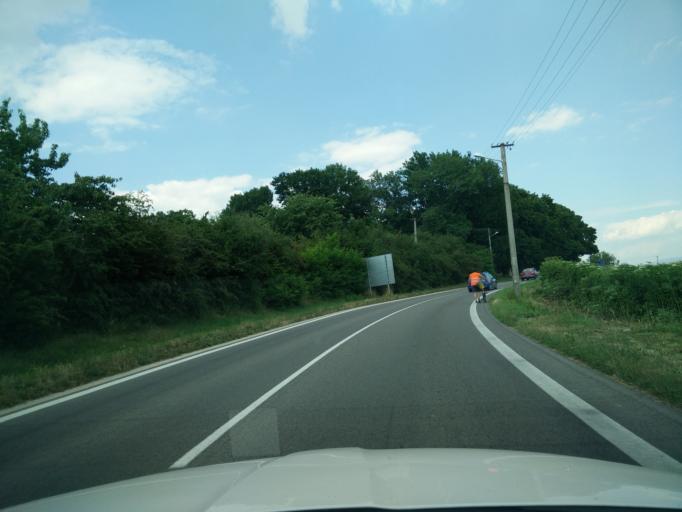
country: SK
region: Nitriansky
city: Partizanske
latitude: 48.6277
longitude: 18.3048
